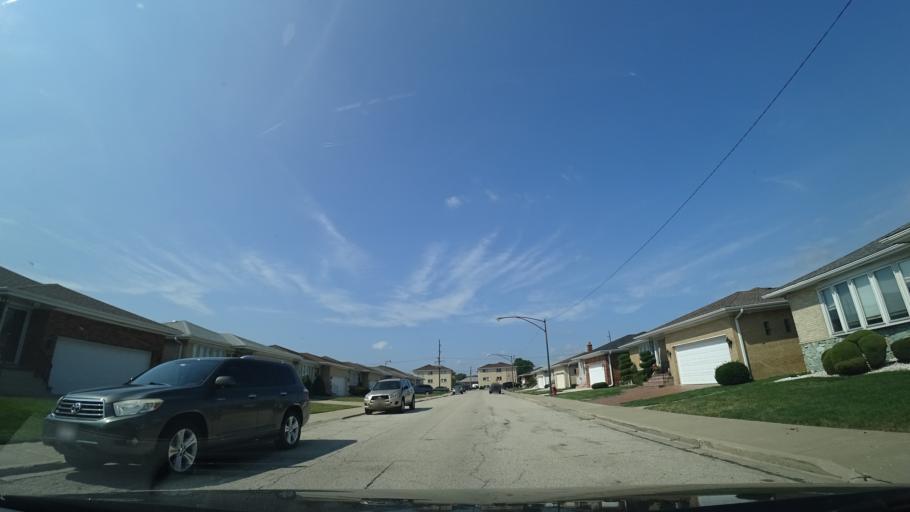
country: US
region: Illinois
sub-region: Cook County
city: Norridge
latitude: 41.9655
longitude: -87.8407
